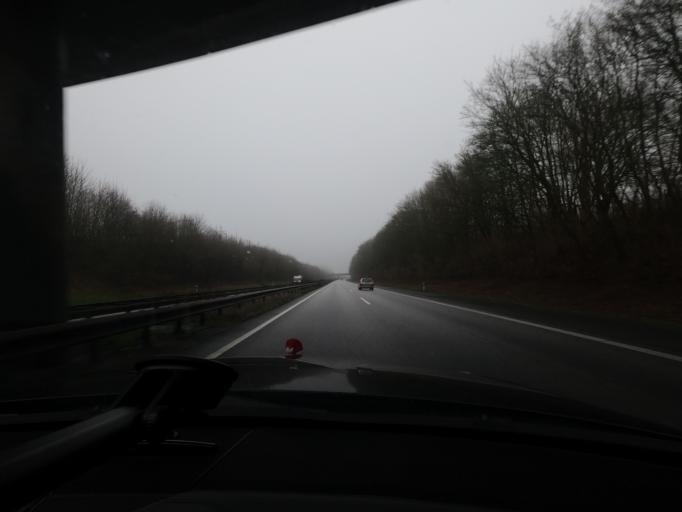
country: DE
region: Schleswig-Holstein
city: Dannewerk
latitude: 54.4977
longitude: 9.5149
